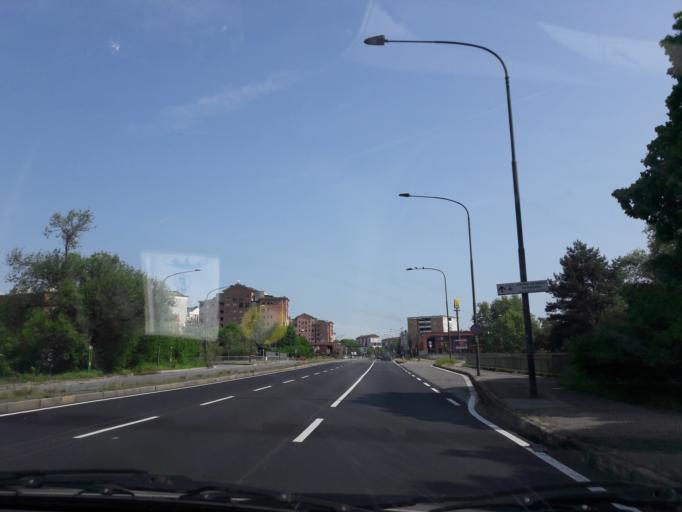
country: IT
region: Piedmont
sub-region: Provincia di Torino
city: Savonera
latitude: 45.0925
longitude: 7.6319
